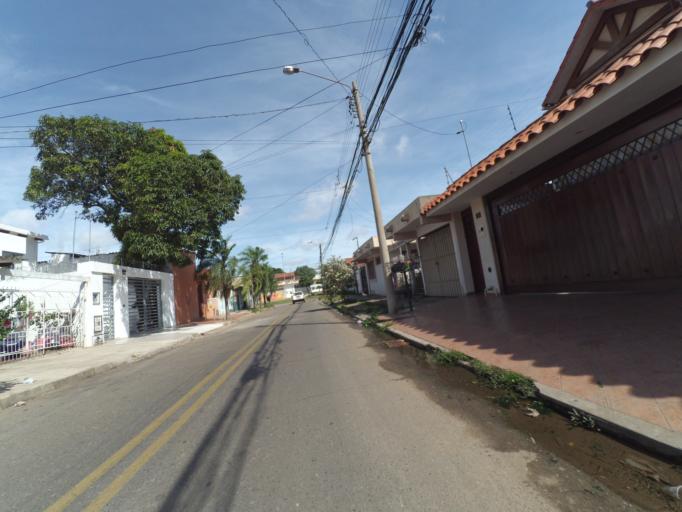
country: BO
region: Santa Cruz
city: Santa Cruz de la Sierra
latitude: -17.7680
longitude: -63.1516
